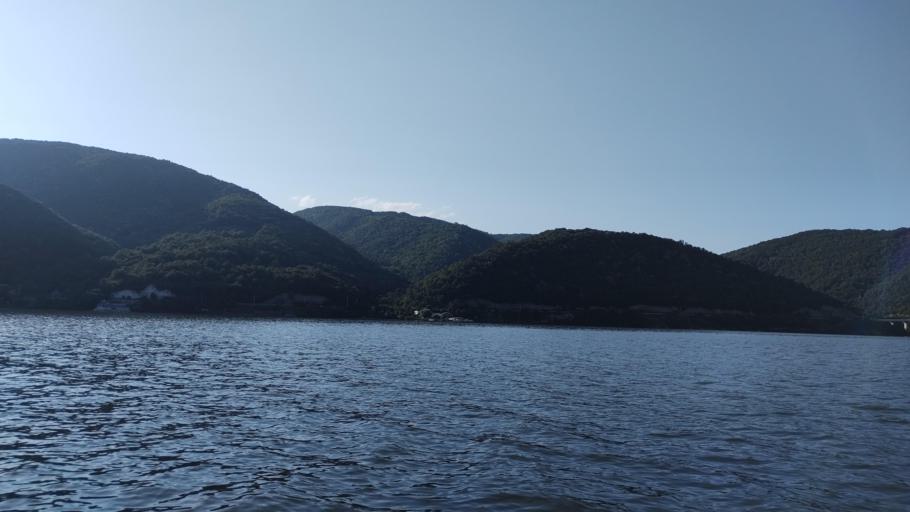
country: RO
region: Mehedinti
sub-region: Comuna Dubova
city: Dubova
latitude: 44.5760
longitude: 22.2450
